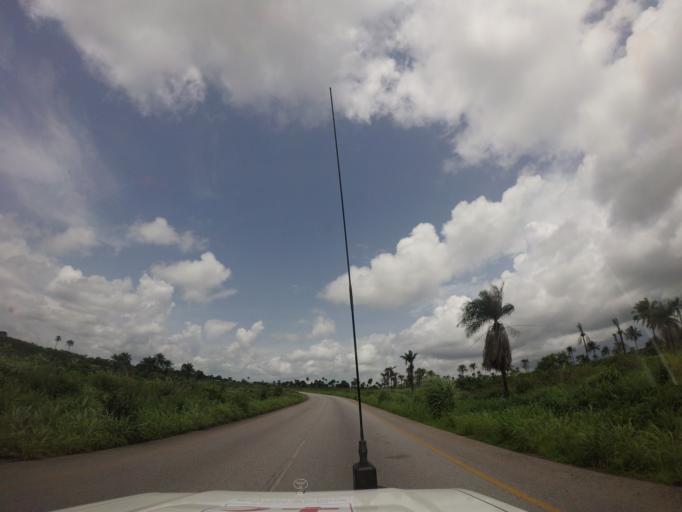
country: SL
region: Northern Province
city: Lunsar
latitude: 8.4606
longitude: -12.5340
